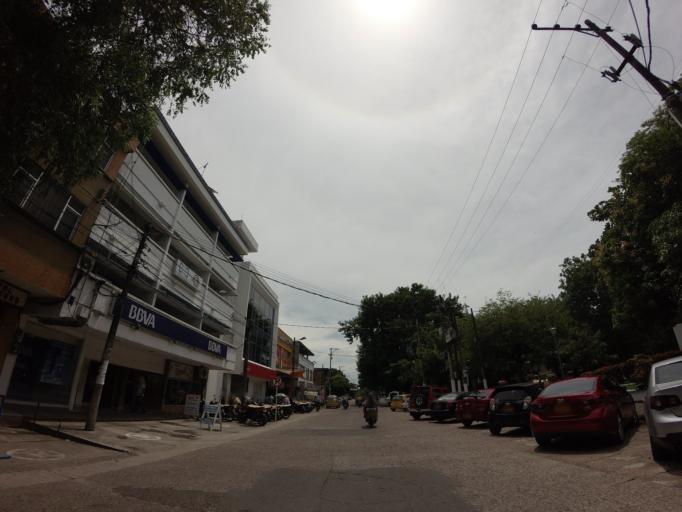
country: CO
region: Caldas
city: La Dorada
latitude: 5.4528
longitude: -74.6623
